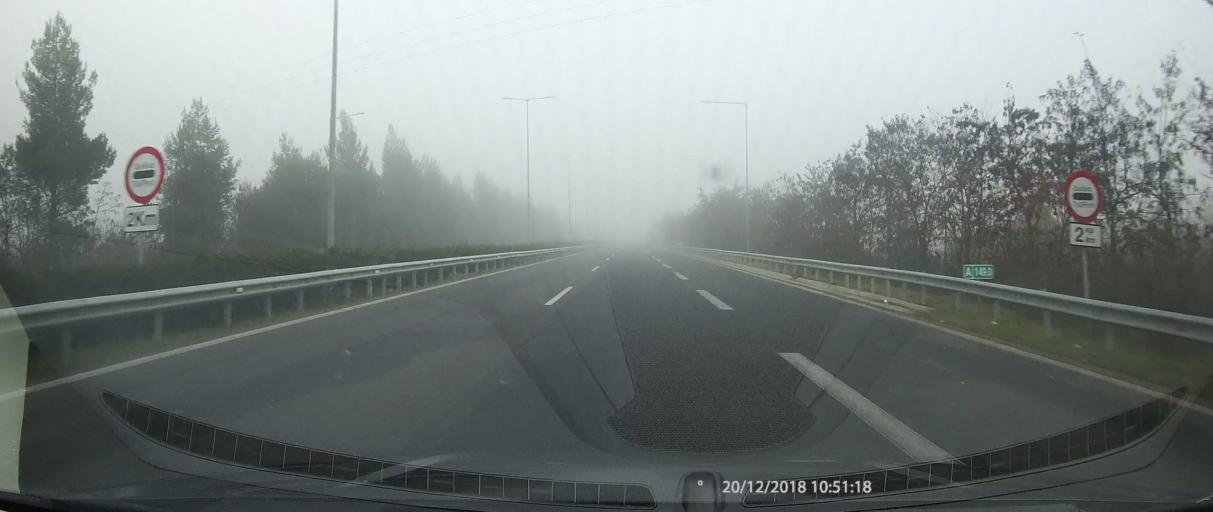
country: GR
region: Peloponnese
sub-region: Nomos Arkadias
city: Tripoli
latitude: 37.5830
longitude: 22.4329
